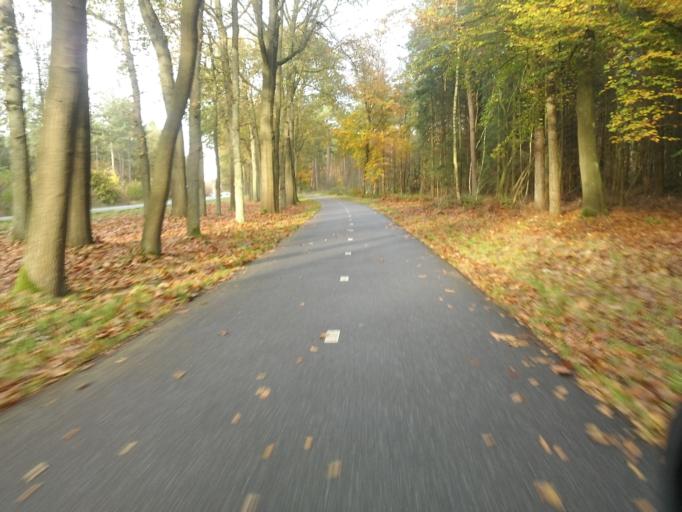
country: NL
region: Utrecht
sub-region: Gemeente Utrechtse Heuvelrug
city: Maarn
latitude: 52.0777
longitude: 5.3602
